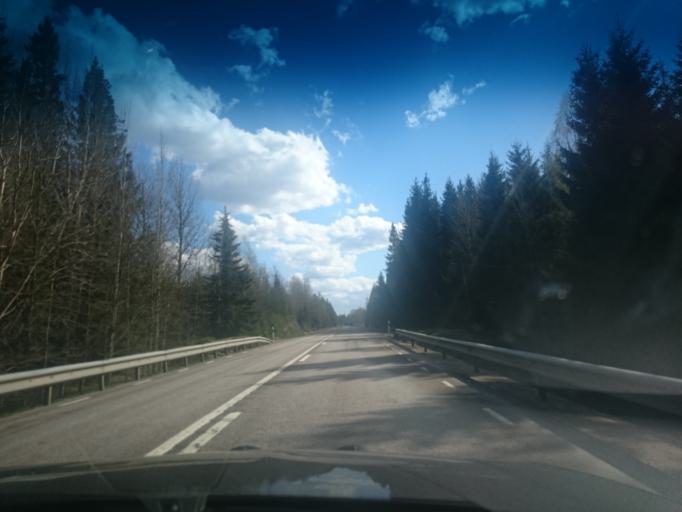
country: SE
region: Joenkoeping
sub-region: Vetlanda Kommun
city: Vetlanda
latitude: 57.2671
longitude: 15.1283
